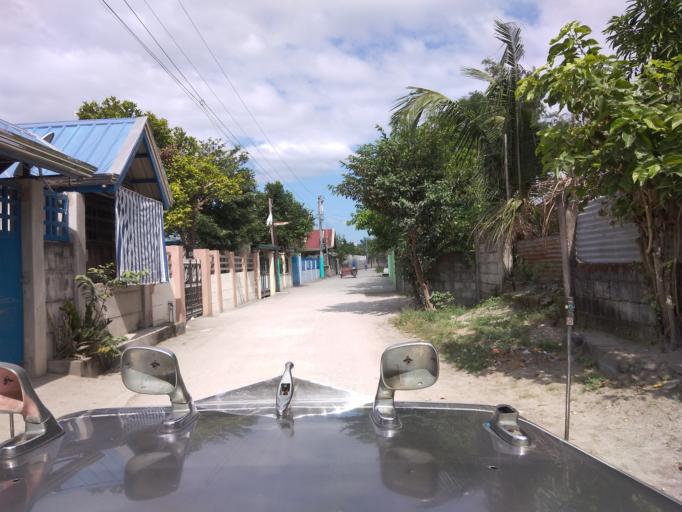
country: PH
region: Central Luzon
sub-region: Province of Pampanga
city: San Patricio
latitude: 15.1097
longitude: 120.7194
